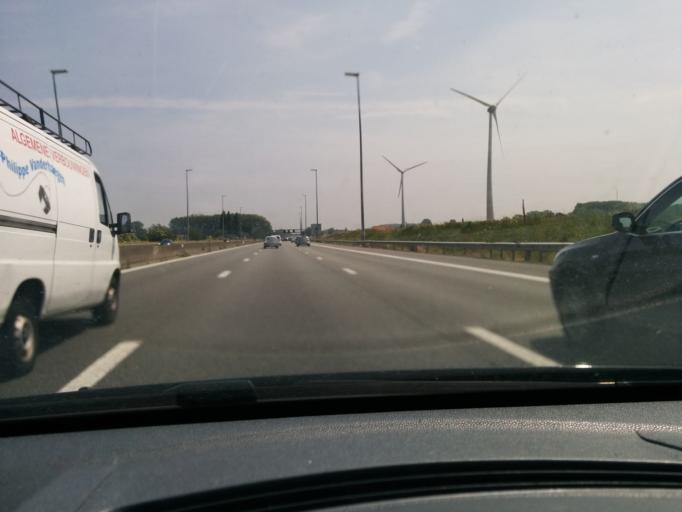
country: BE
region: Flanders
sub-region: Provincie Oost-Vlaanderen
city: Melle
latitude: 50.9850
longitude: 3.8127
